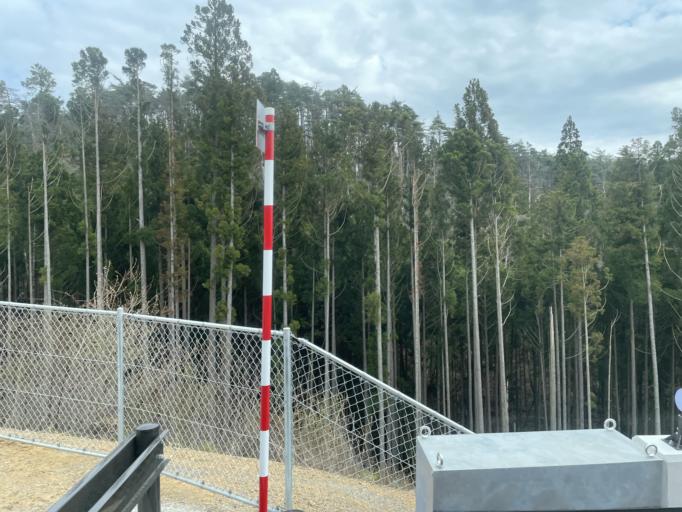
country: JP
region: Iwate
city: Ofunato
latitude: 38.9207
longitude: 141.5946
